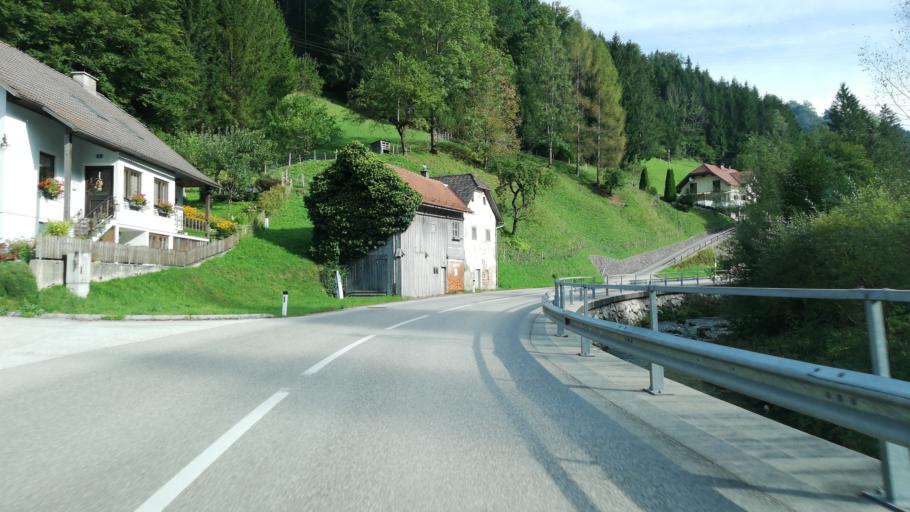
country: AT
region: Upper Austria
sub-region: Politischer Bezirk Steyr-Land
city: Maria Neustift
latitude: 47.8965
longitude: 14.5461
